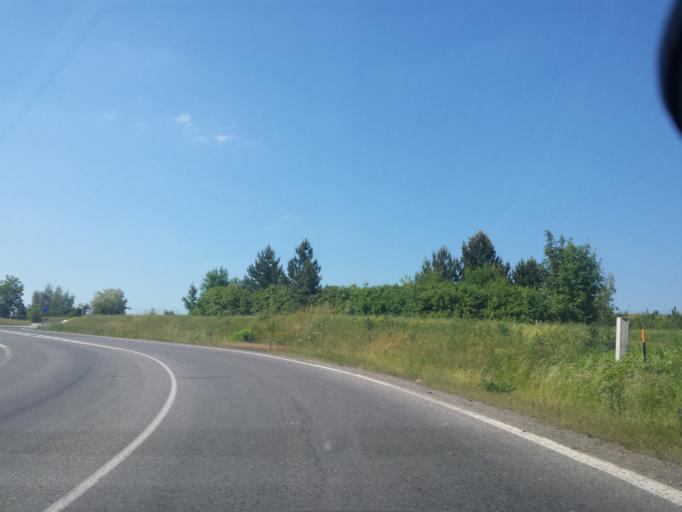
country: CZ
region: Central Bohemia
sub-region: Okres Melnik
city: Veltrusy
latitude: 50.3099
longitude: 14.3155
